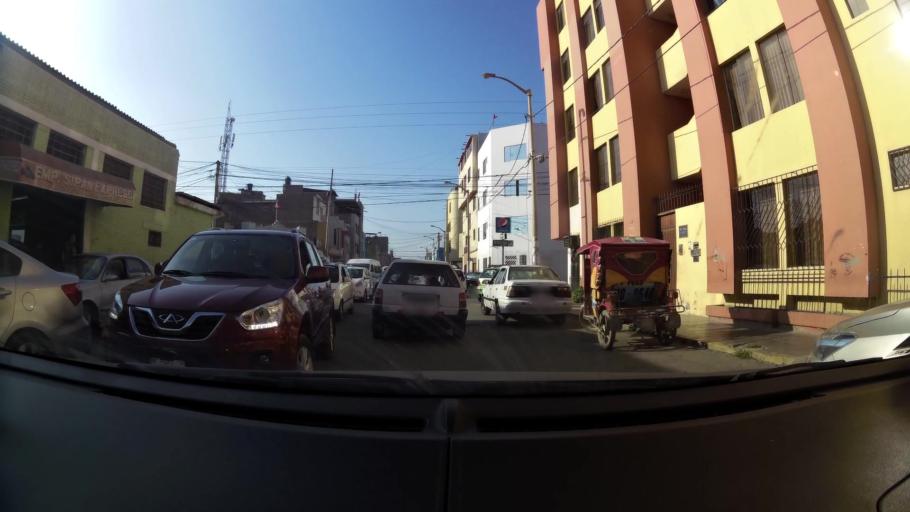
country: PE
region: Lambayeque
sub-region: Provincia de Chiclayo
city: Chiclayo
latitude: -6.7703
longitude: -79.8447
